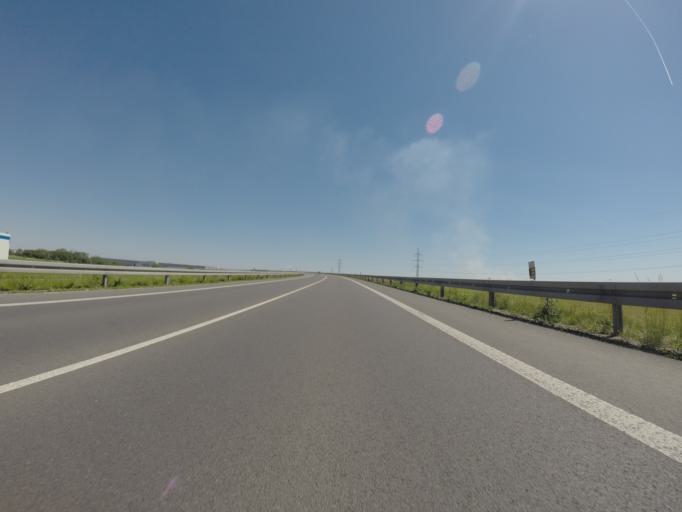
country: SK
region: Trnavsky
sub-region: Okres Galanta
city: Galanta
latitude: 48.1797
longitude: 17.7376
